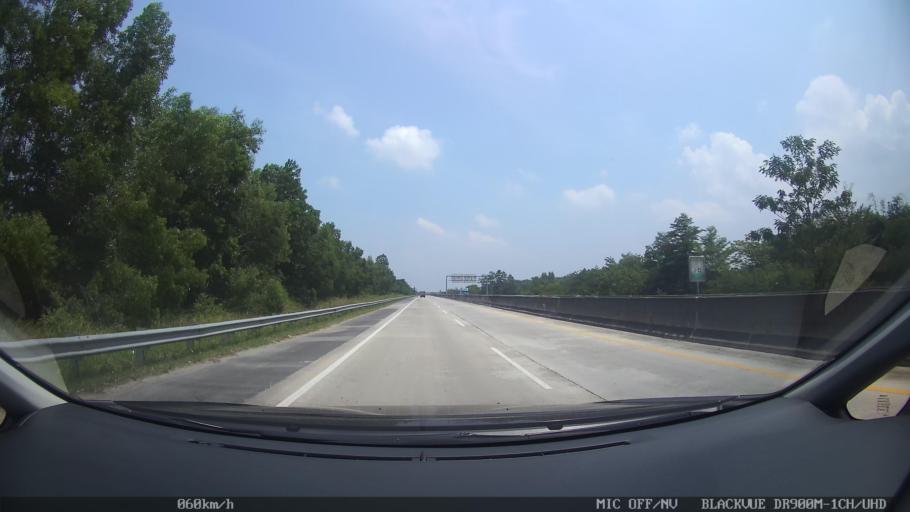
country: ID
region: Lampung
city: Kedaton
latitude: -5.3839
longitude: 105.3359
